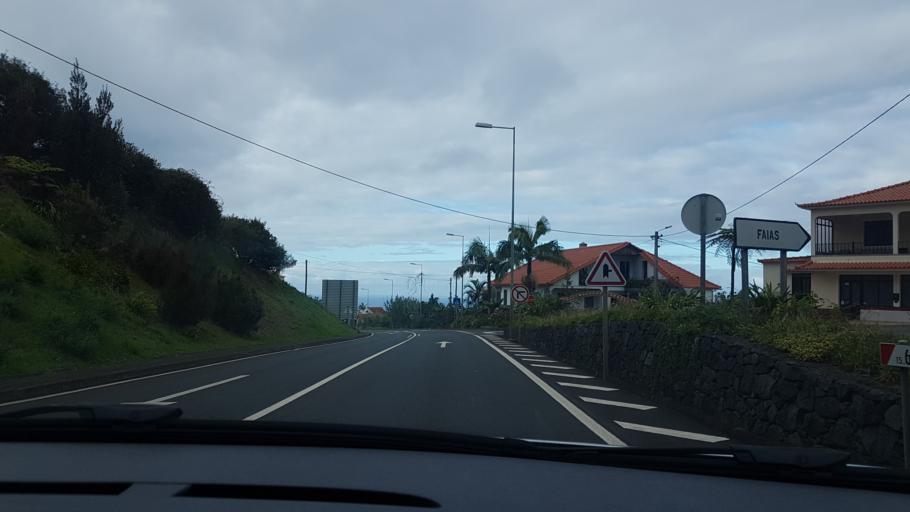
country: PT
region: Madeira
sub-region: Santana
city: Santana
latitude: 32.8122
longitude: -16.8853
